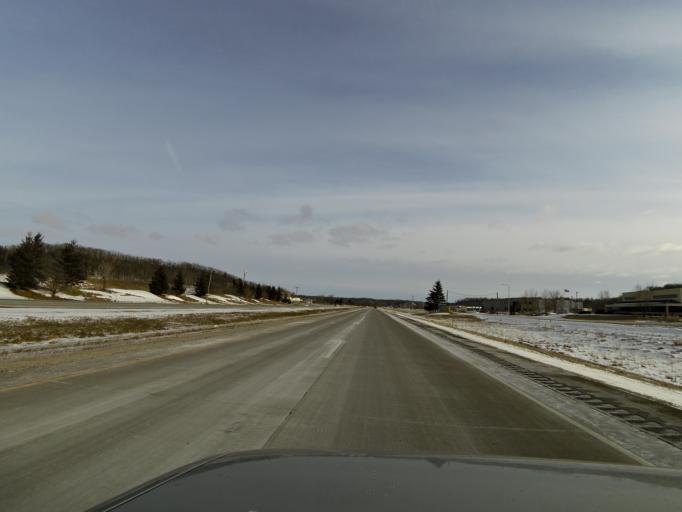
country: US
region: Wisconsin
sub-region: Pierce County
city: River Falls
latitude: 44.8923
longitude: -92.6374
